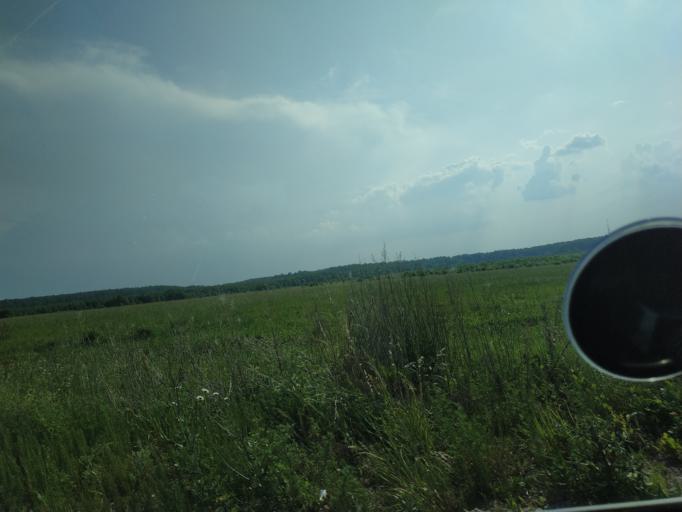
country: RU
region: Moskovskaya
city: Yakovlevskoye
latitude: 55.4283
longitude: 37.9454
